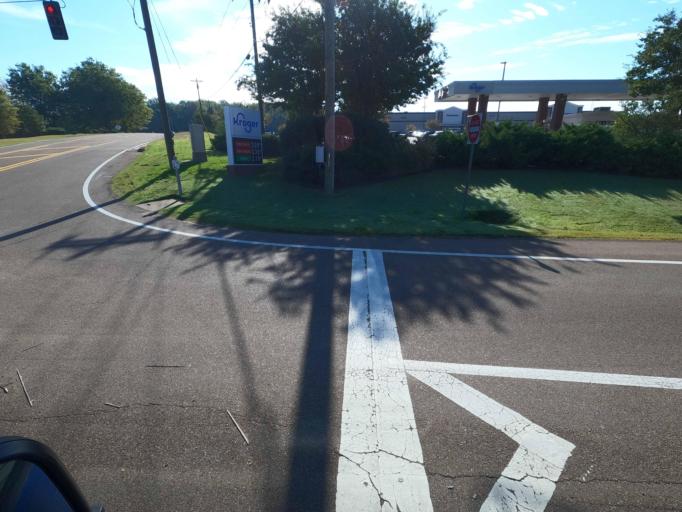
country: US
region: Tennessee
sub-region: Tipton County
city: Atoka
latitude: 35.4420
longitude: -89.7914
